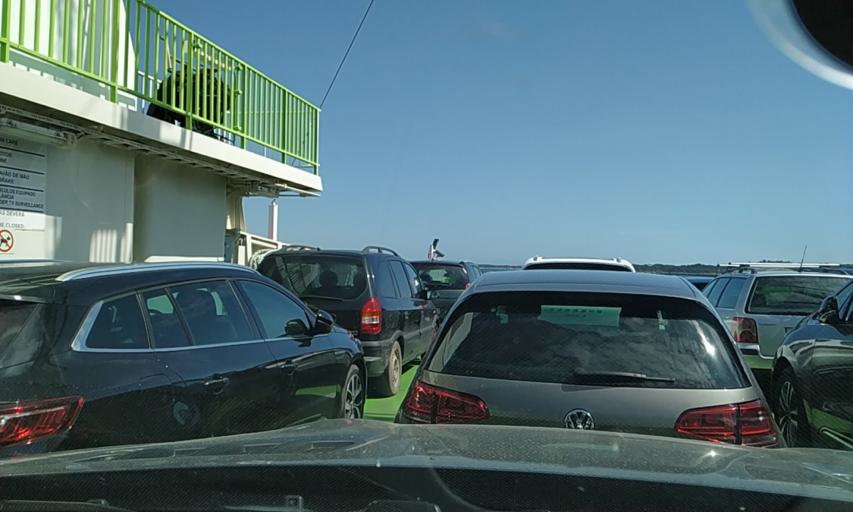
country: PT
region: Setubal
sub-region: Setubal
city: Setubal
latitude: 38.4827
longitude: -8.8741
